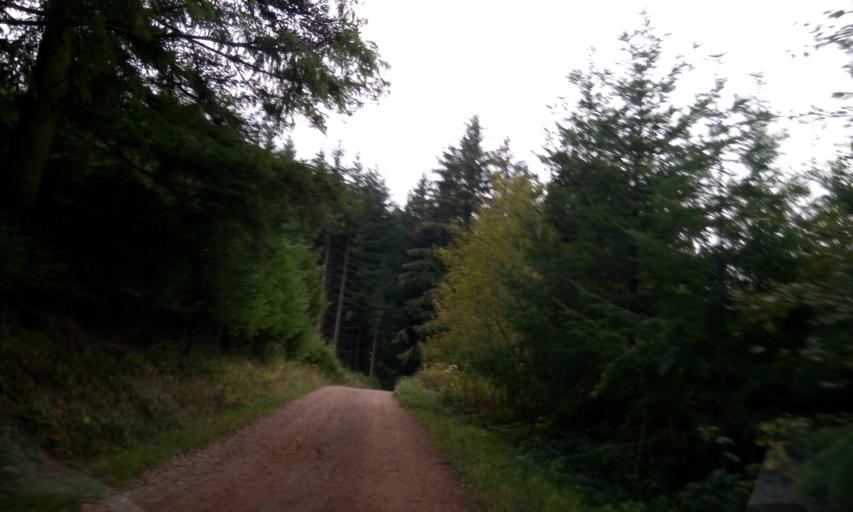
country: FR
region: Rhone-Alpes
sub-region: Departement du Rhone
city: Cublize
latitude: 46.0164
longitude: 4.4259
